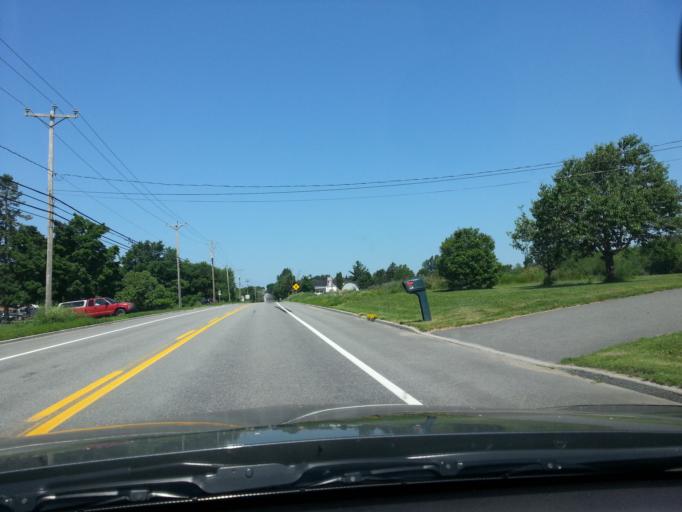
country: CA
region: Ontario
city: Bells Corners
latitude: 45.4272
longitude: -75.8971
